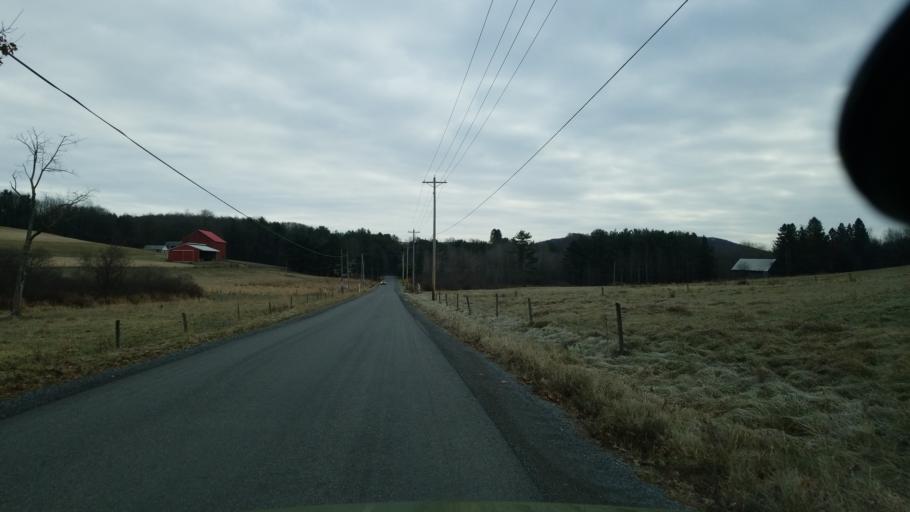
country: US
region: Pennsylvania
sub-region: Clearfield County
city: Treasure Lake
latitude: 41.1108
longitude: -78.6531
